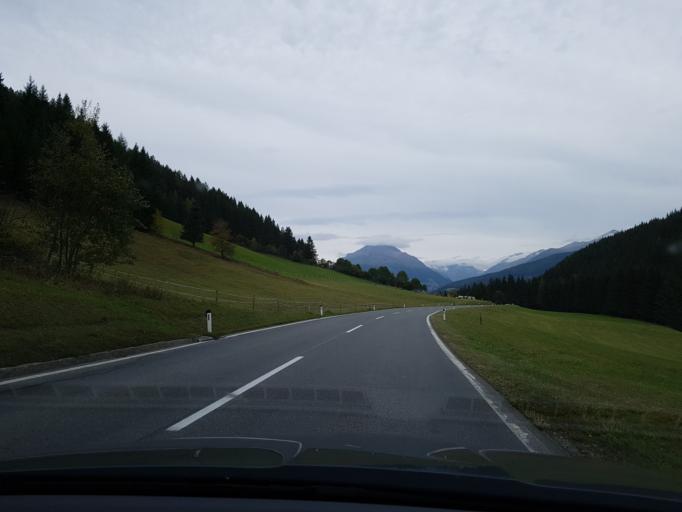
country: AT
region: Salzburg
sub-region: Politischer Bezirk Tamsweg
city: Tamsweg
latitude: 47.1101
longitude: 13.8155
